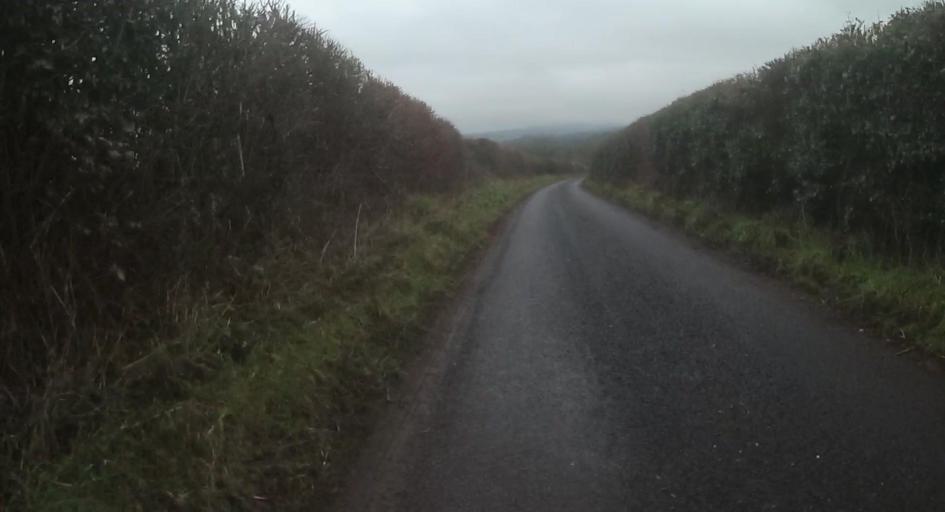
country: GB
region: England
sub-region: Hampshire
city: Kings Worthy
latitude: 51.0985
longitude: -1.2524
